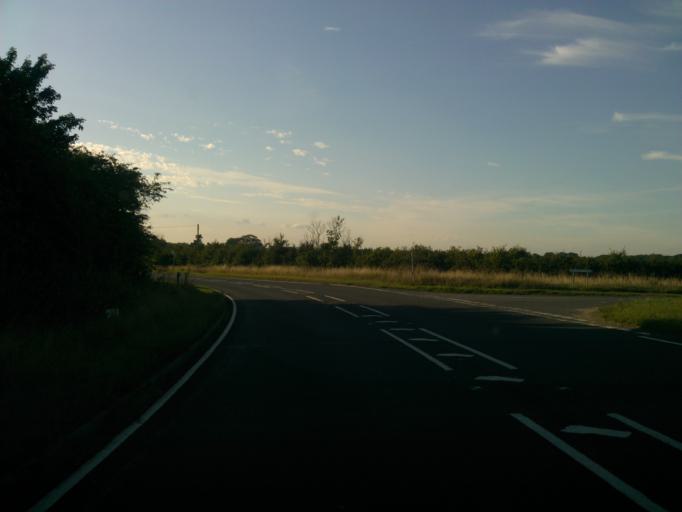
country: GB
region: England
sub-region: Essex
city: Saint Osyth
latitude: 51.8190
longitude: 1.0737
